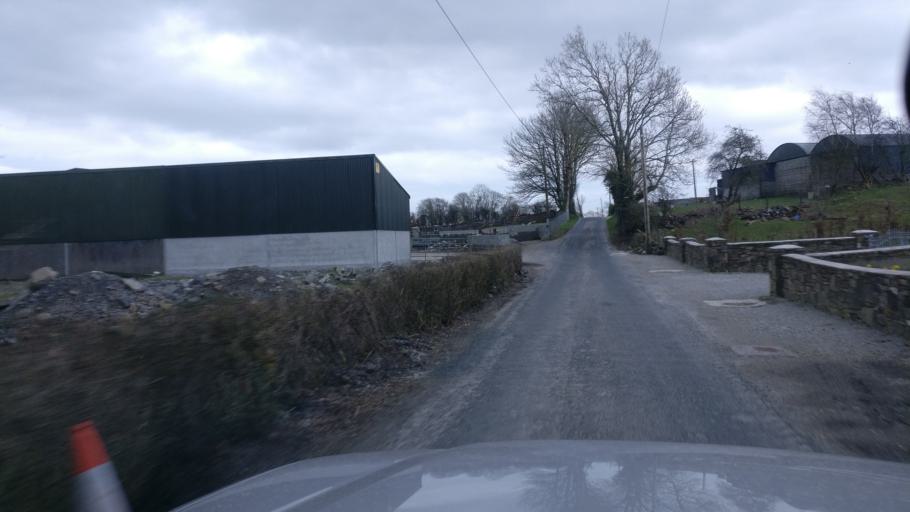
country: IE
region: Connaught
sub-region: County Galway
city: Loughrea
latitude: 53.2584
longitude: -8.4474
